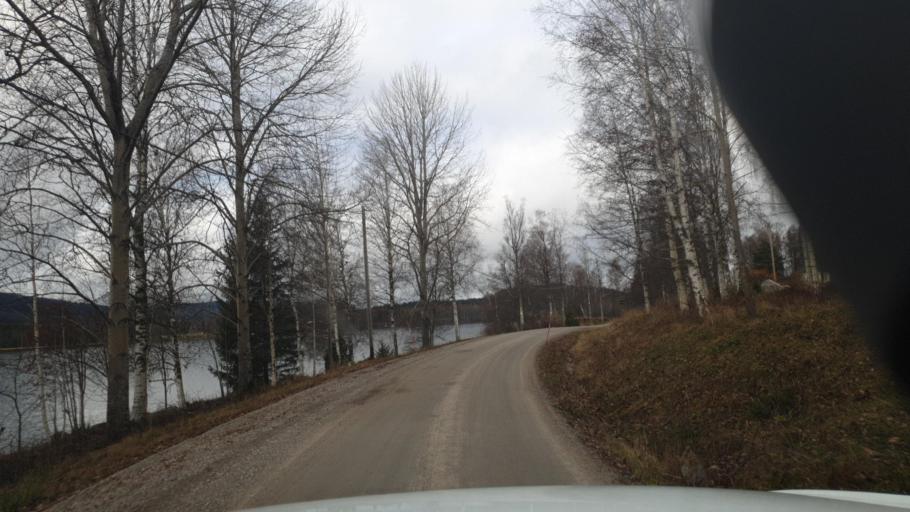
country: SE
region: Vaermland
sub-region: Arvika Kommun
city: Arvika
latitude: 59.7353
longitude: 12.8309
